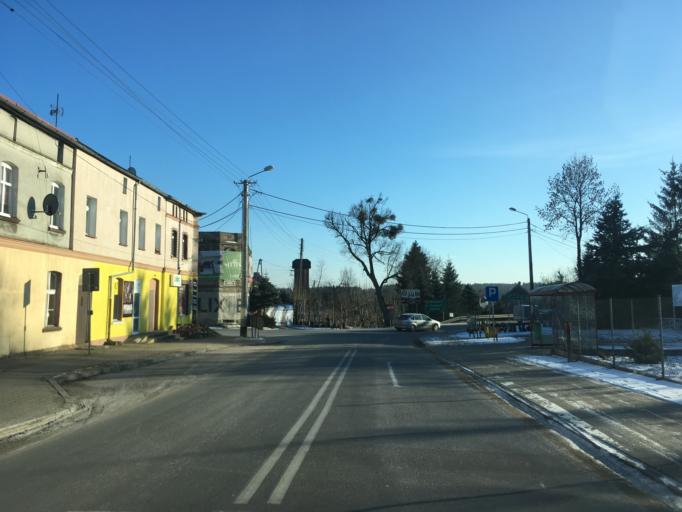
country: PL
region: Pomeranian Voivodeship
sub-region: Powiat starogardzki
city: Zblewo
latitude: 53.8893
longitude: 18.3507
